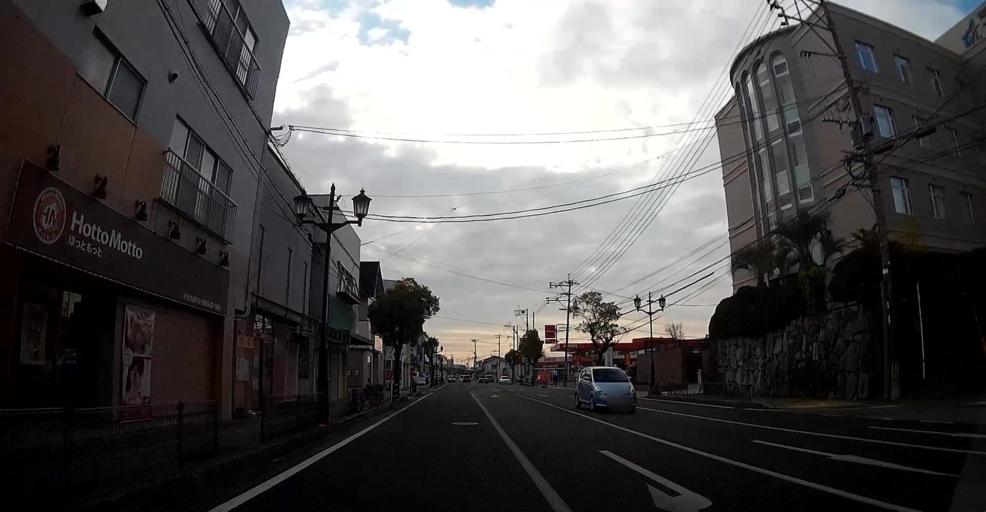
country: JP
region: Kumamoto
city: Hondo
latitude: 32.4494
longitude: 130.1994
